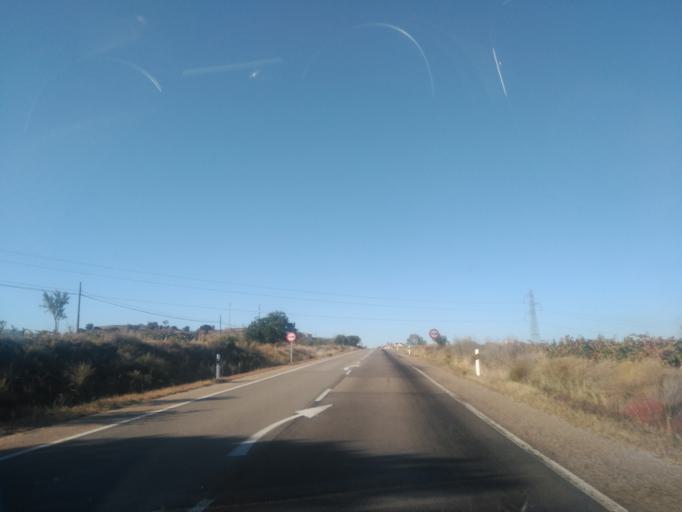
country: ES
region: Castille and Leon
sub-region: Provincia de Burgos
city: Castrillo de la Vega
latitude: 41.6561
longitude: -3.7699
